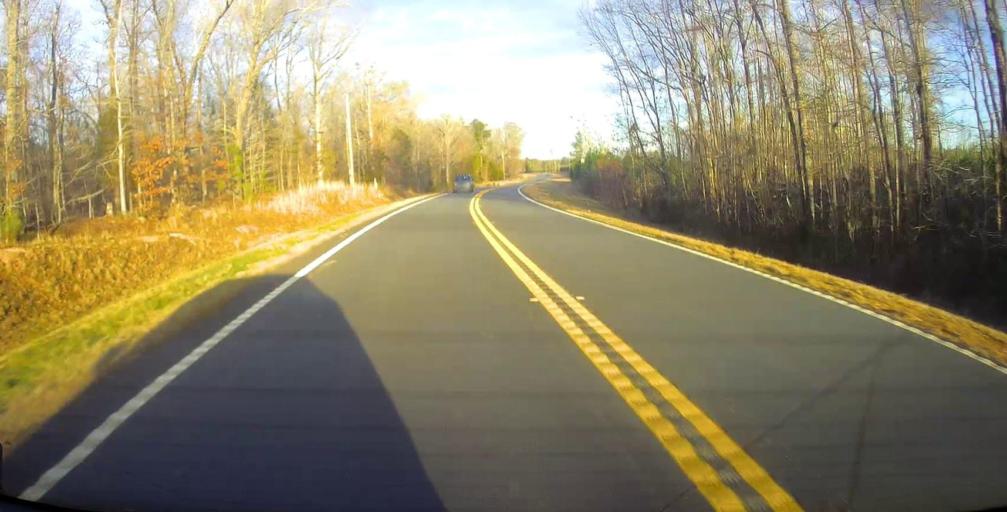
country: US
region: Georgia
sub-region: Talbot County
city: Sardis
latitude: 32.7215
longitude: -84.6571
